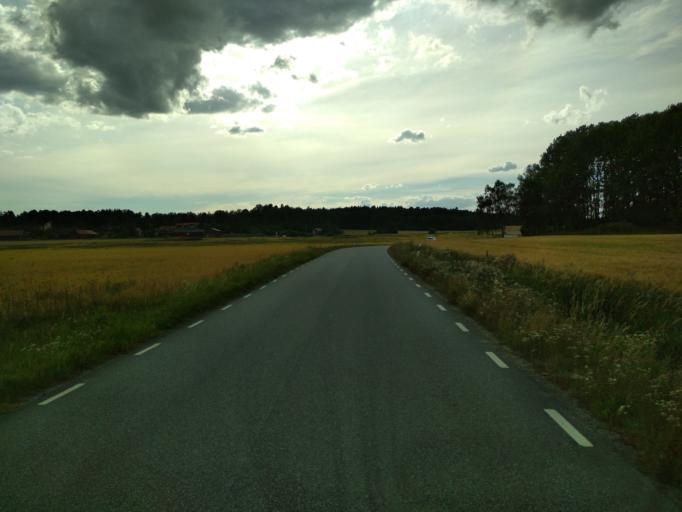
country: SE
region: Uppsala
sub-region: Habo Kommun
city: Balsta
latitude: 59.6655
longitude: 17.5638
